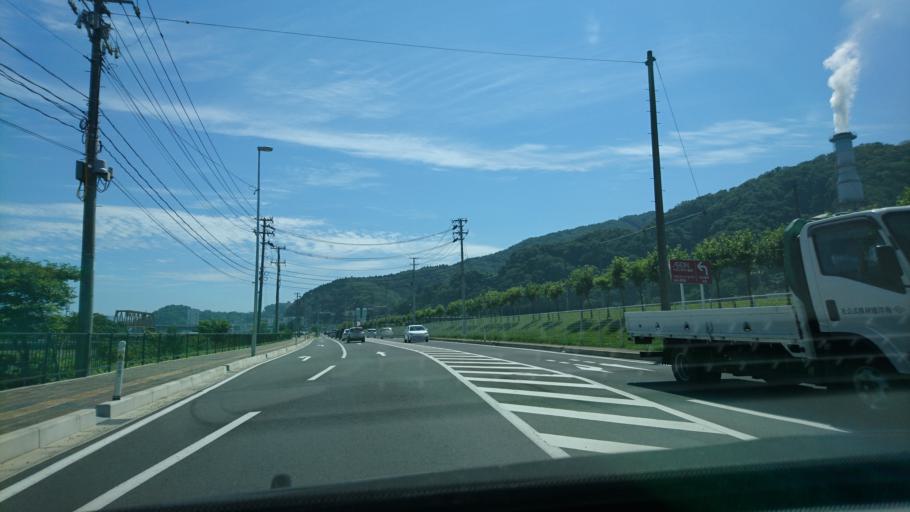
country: JP
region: Iwate
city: Kamaishi
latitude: 39.2705
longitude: 141.8769
